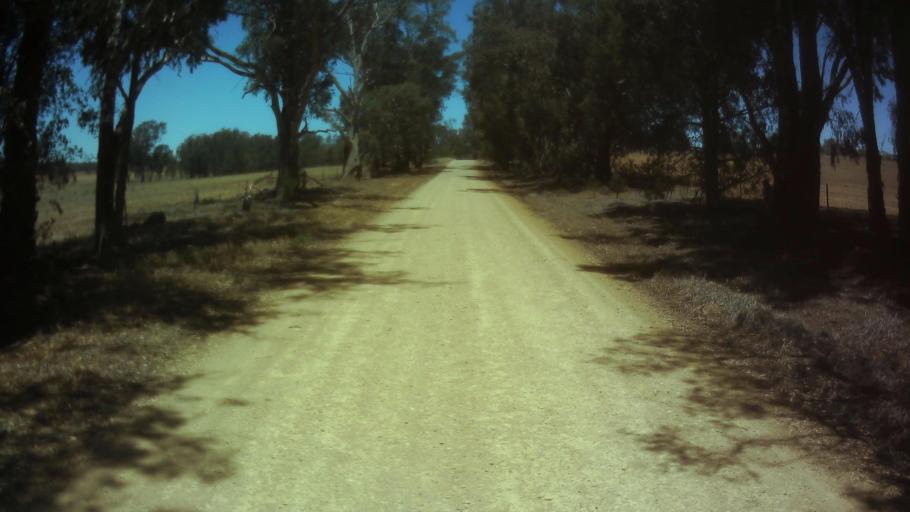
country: AU
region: New South Wales
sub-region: Weddin
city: Grenfell
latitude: -33.9113
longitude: 148.2141
